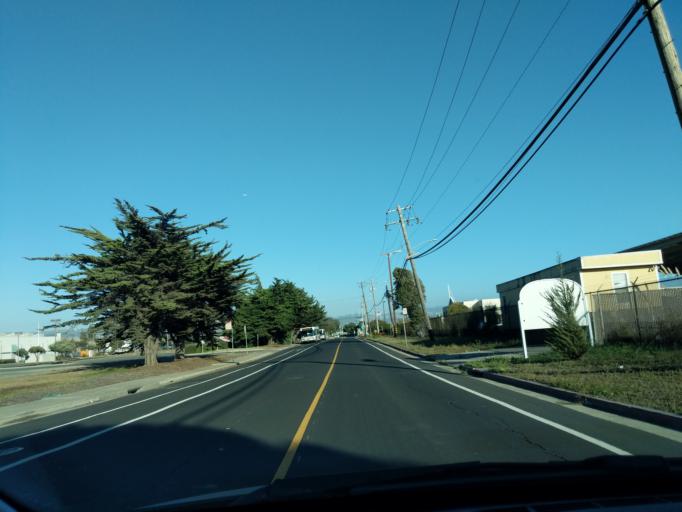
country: US
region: California
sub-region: Contra Costa County
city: Richmond
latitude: 37.9138
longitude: -122.3582
